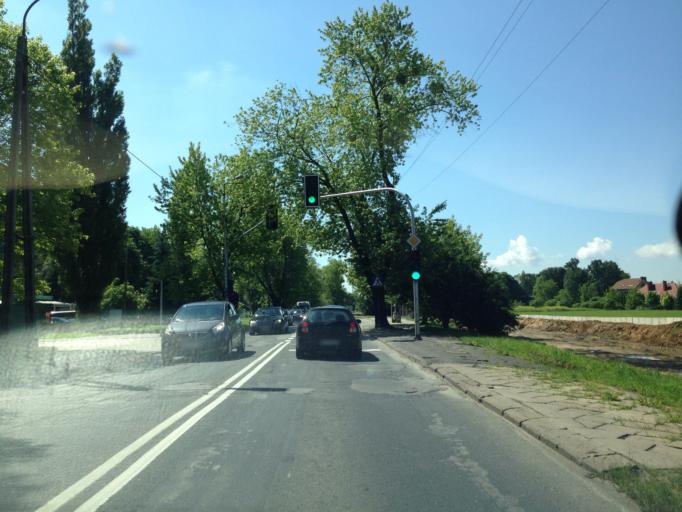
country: PL
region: Masovian Voivodeship
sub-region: Warszawa
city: Ursus
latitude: 52.2244
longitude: 20.8972
